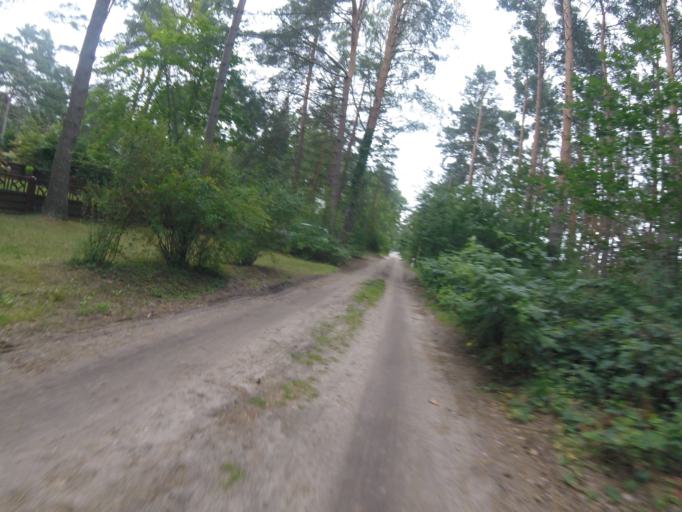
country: DE
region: Brandenburg
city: Mittenwalde
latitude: 52.2225
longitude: 13.5756
